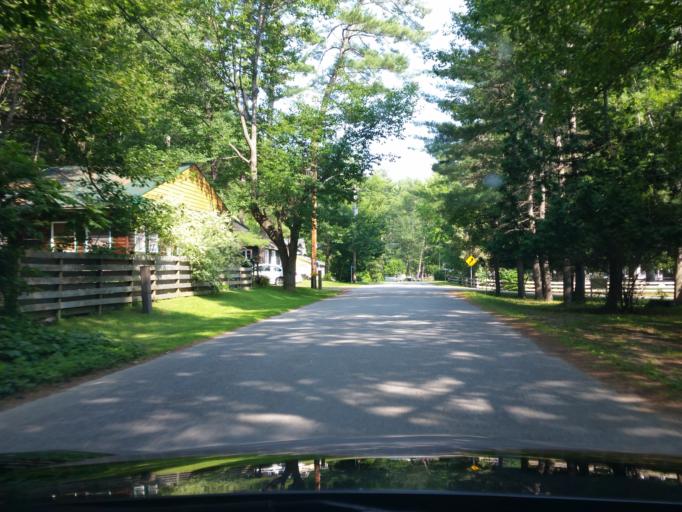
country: CA
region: Quebec
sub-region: Outaouais
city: Shawville
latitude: 45.5191
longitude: -76.4226
